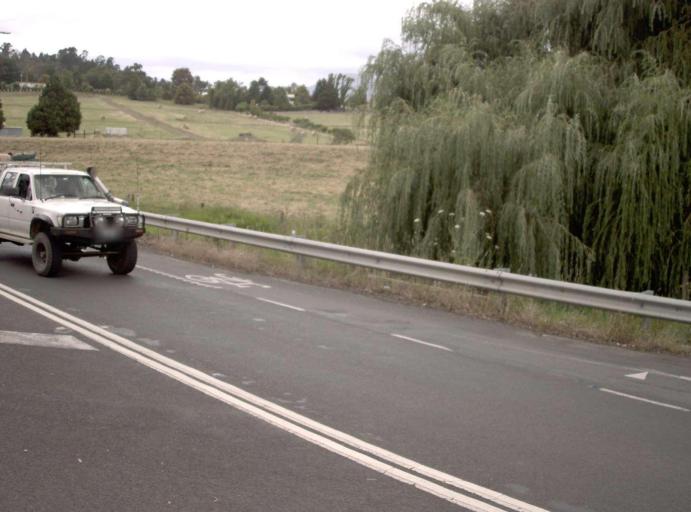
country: AU
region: Victoria
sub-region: Yarra Ranges
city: Healesville
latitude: -37.6723
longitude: 145.5106
